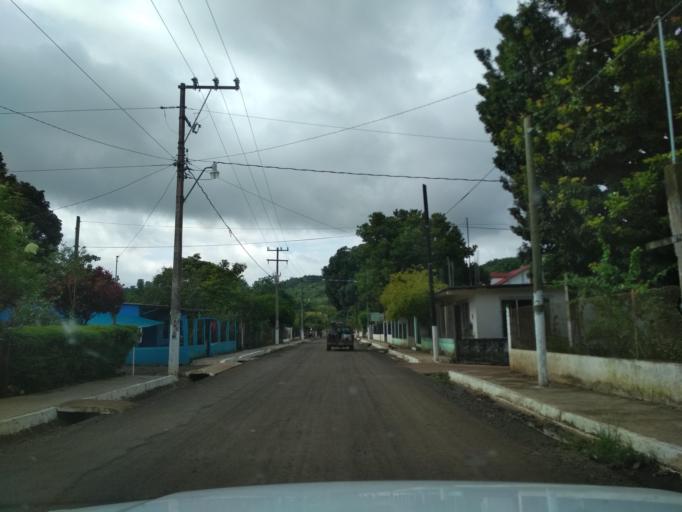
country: MX
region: Veracruz
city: Catemaco
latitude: 18.3763
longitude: -95.1244
